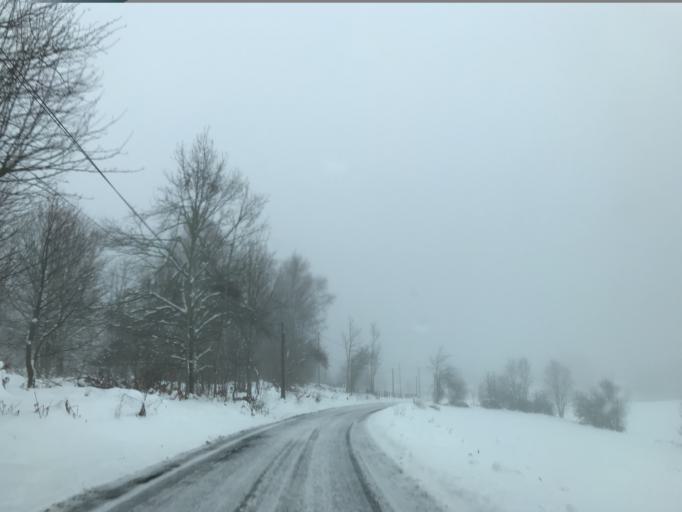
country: FR
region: Rhone-Alpes
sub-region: Departement de la Loire
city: Noiretable
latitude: 45.7281
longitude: 3.6969
